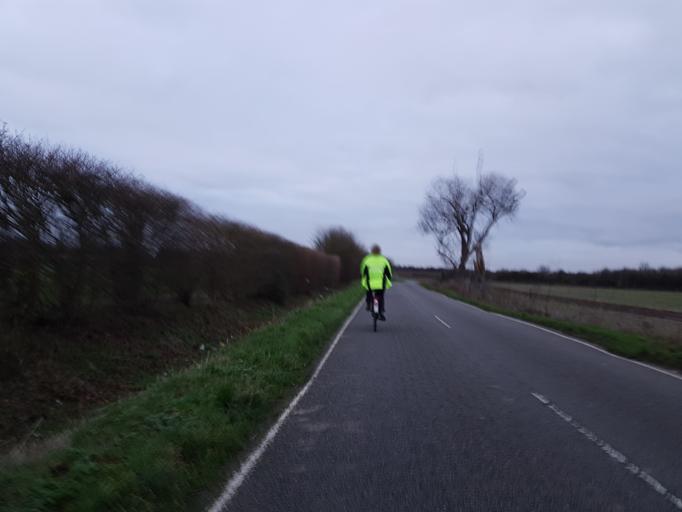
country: GB
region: England
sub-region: Cambridgeshire
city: Fulbourn
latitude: 52.2150
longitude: 0.1949
